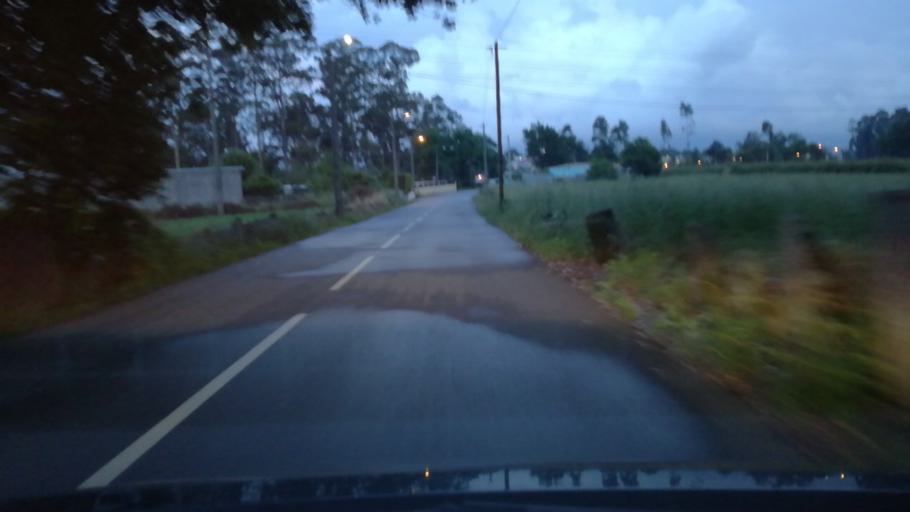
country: PT
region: Porto
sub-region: Maia
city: Maia
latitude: 41.2534
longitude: -8.6122
